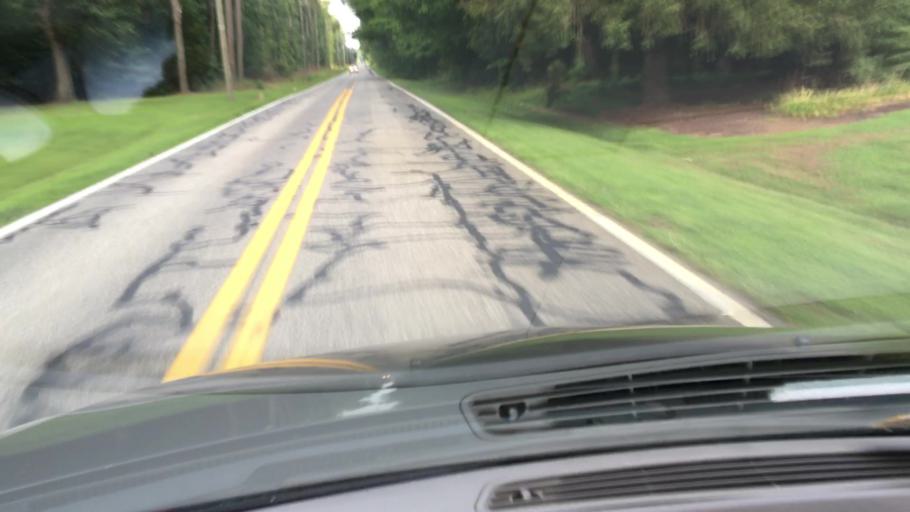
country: US
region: Delaware
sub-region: Sussex County
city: Ocean View
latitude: 38.5153
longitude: -75.0884
